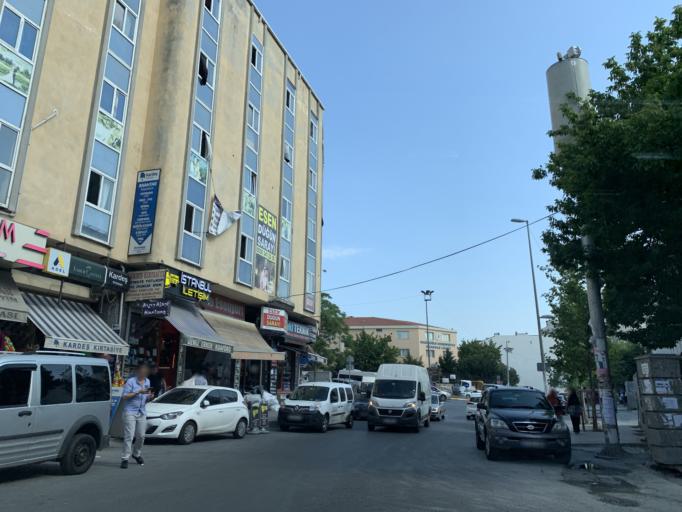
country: TR
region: Istanbul
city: Esenyurt
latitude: 41.0343
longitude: 28.6772
